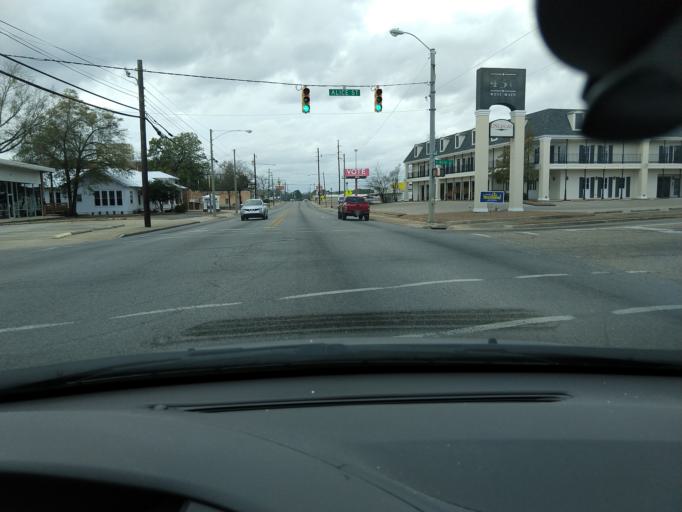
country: US
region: Alabama
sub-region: Houston County
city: Dothan
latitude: 31.2245
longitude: -85.3971
